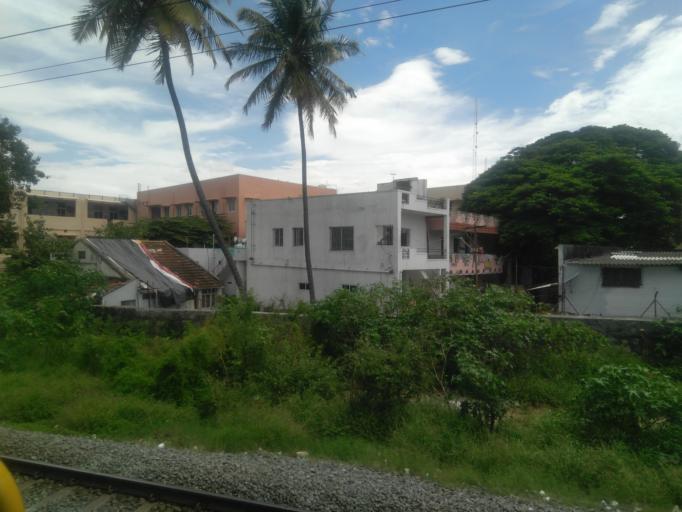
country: IN
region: Tamil Nadu
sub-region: Coimbatore
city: Coimbatore
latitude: 11.0132
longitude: 76.9576
